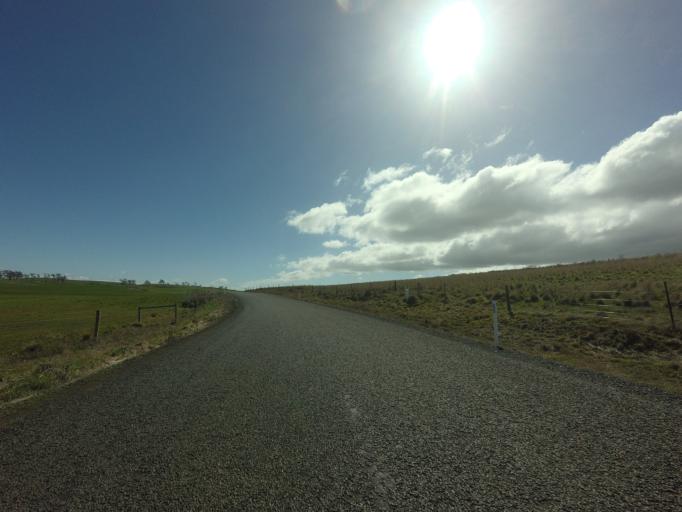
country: AU
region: Tasmania
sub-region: Northern Midlands
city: Evandale
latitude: -41.9149
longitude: 147.4719
